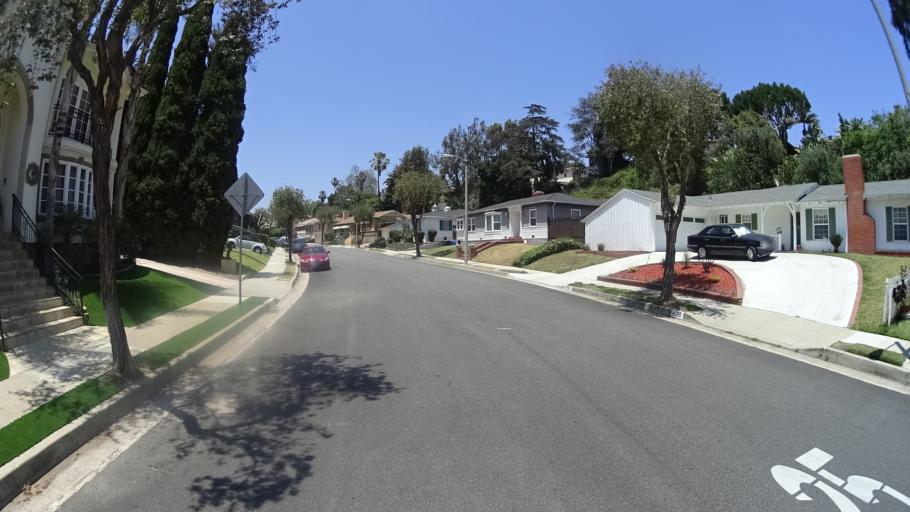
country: US
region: California
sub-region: Los Angeles County
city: View Park-Windsor Hills
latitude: 33.9999
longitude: -118.3376
